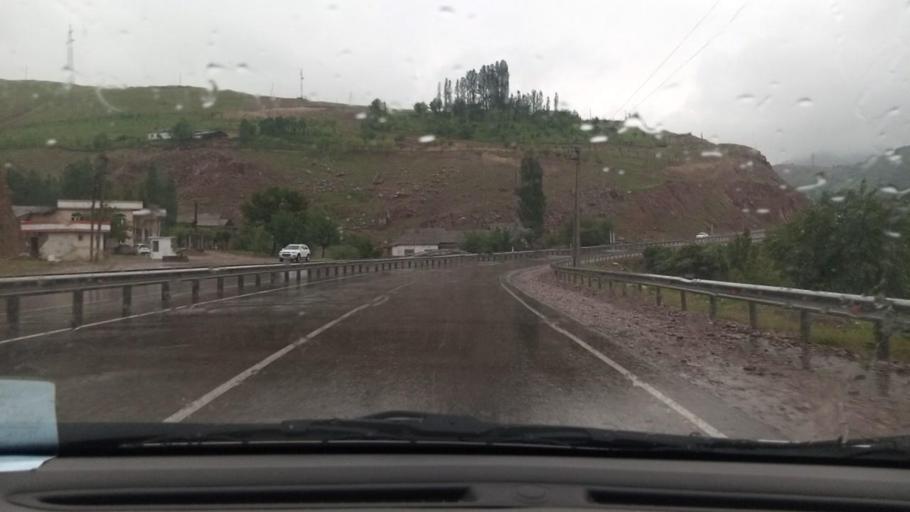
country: UZ
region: Toshkent
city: Angren
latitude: 41.1025
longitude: 70.3300
